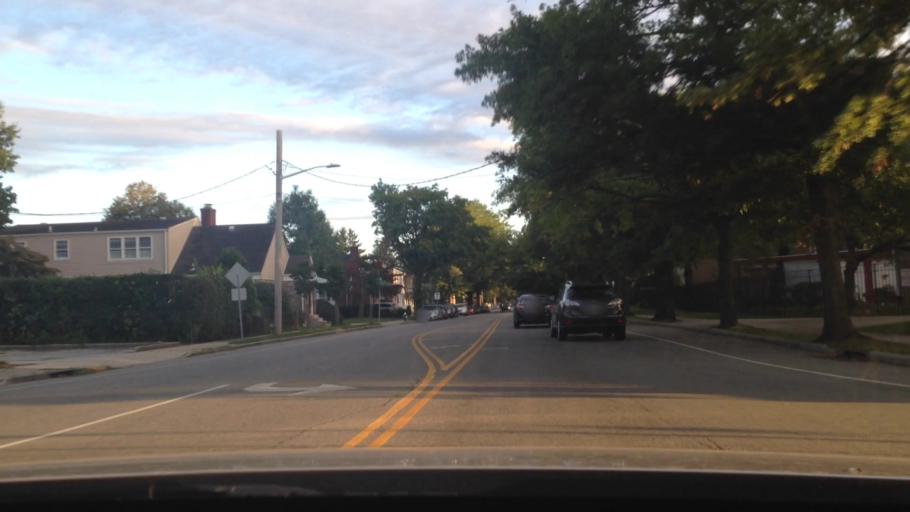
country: US
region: New York
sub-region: Nassau County
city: Garden City South
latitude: 40.7070
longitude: -73.6612
